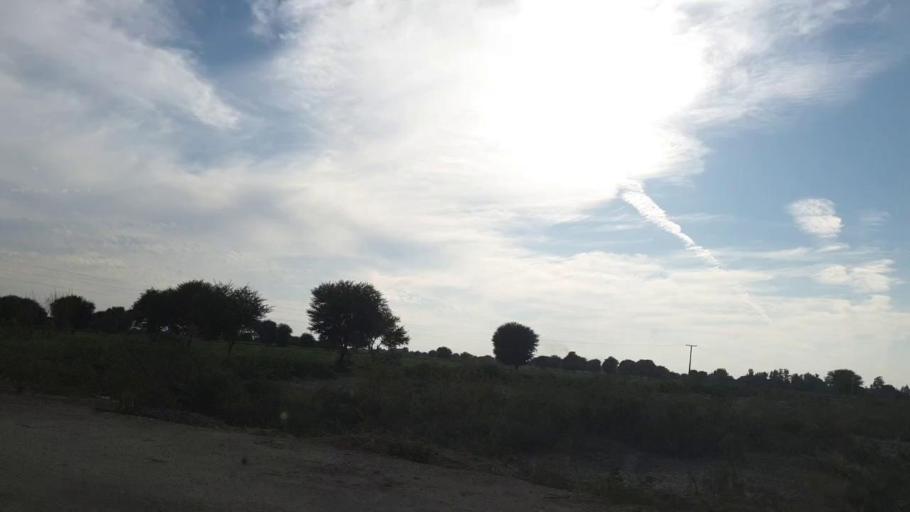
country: PK
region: Sindh
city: Pithoro
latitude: 25.6453
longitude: 69.3614
